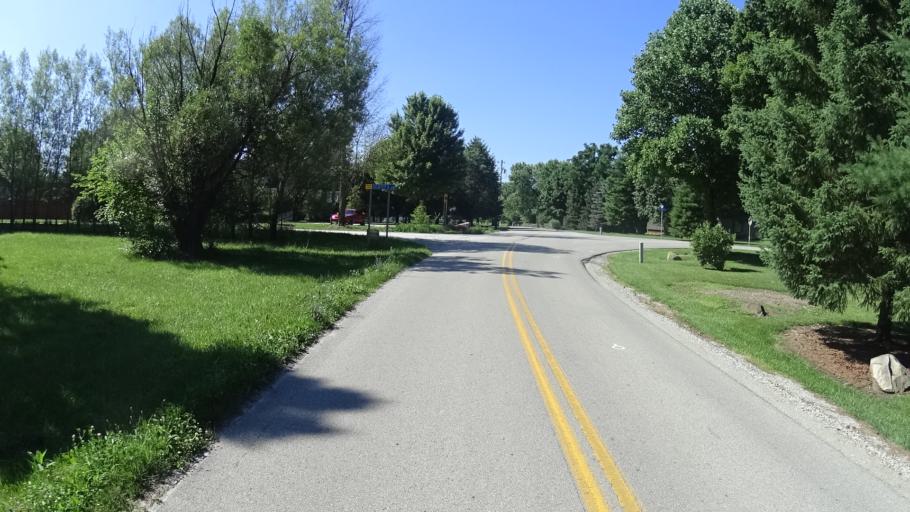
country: US
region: Indiana
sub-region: Madison County
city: Ingalls
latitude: 39.9590
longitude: -85.8151
